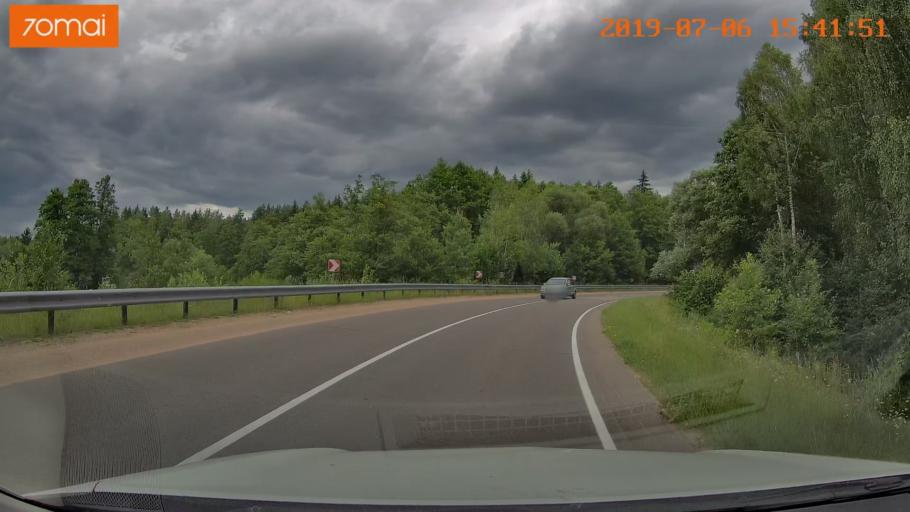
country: BY
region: Minsk
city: Rakaw
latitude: 53.9857
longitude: 26.9880
